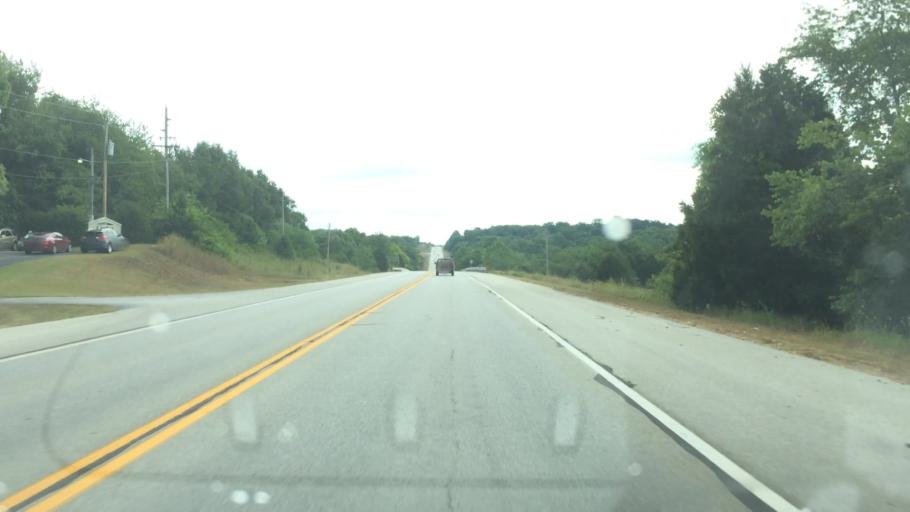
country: US
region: Missouri
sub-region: Greene County
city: Springfield
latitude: 37.1796
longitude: -93.2030
